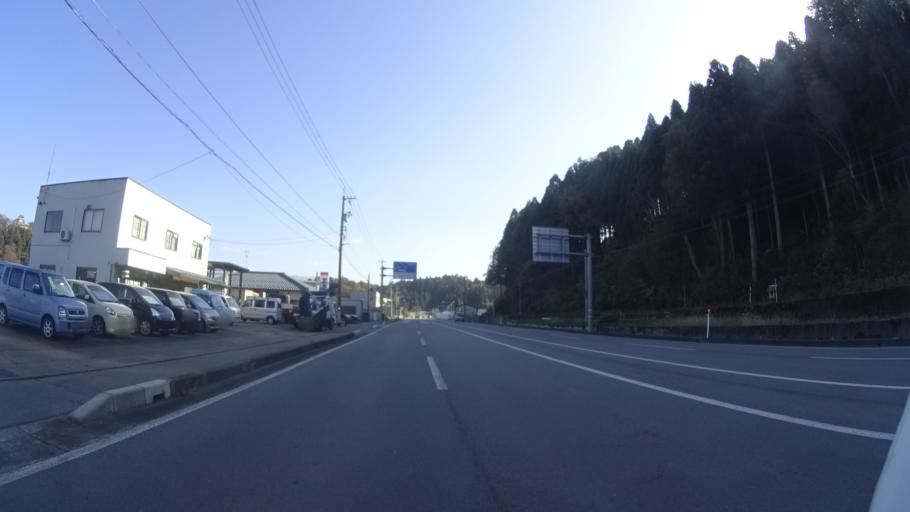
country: JP
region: Fukui
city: Ono
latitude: 35.9869
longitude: 136.4755
